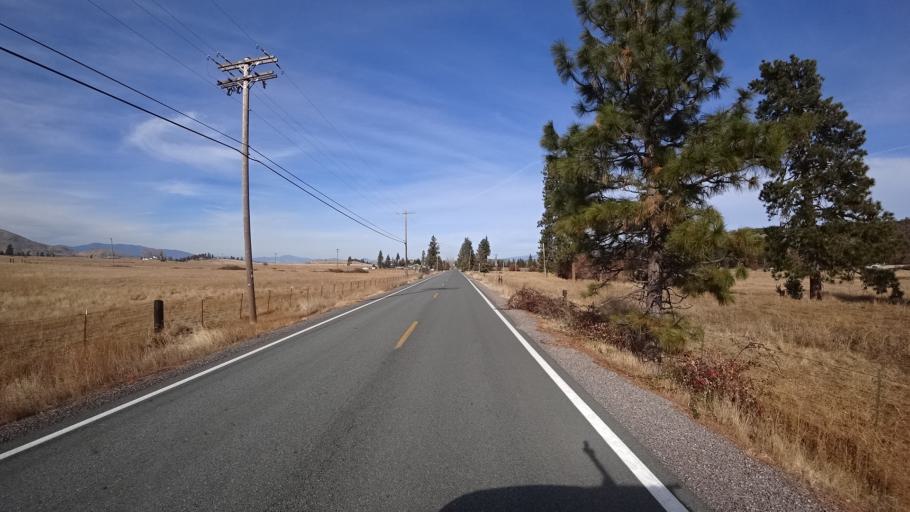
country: US
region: California
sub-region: Siskiyou County
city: Weed
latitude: 41.4358
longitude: -122.4360
